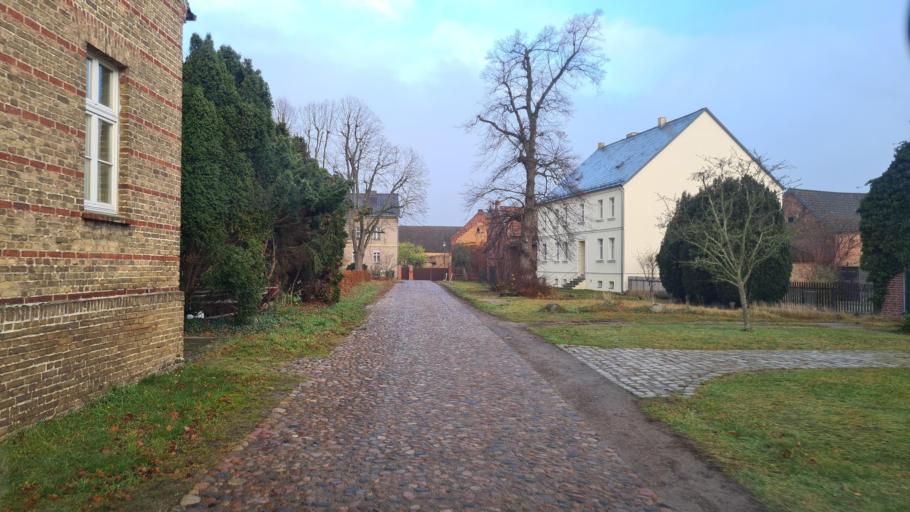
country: DE
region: Brandenburg
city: Beelitz
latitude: 52.1571
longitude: 12.9697
